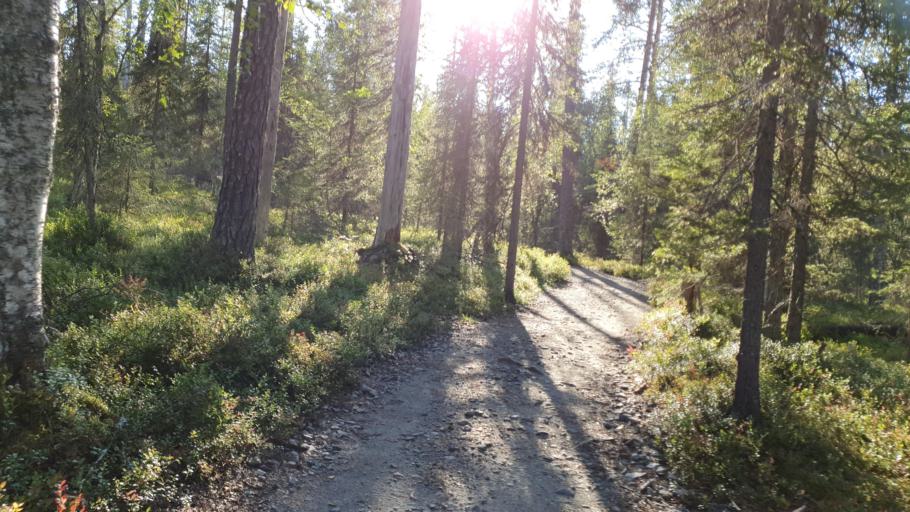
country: FI
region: Lapland
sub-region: Tunturi-Lappi
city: Kolari
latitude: 67.5975
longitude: 24.2205
